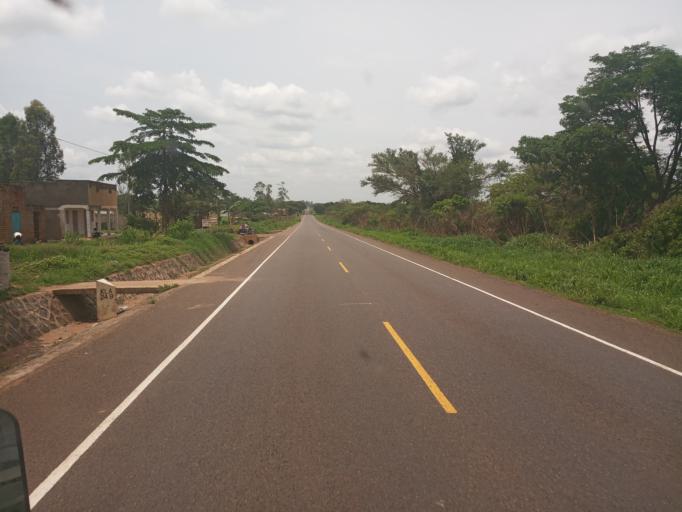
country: UG
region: Northern Region
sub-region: Oyam District
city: Oyam
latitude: 2.1746
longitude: 32.2234
